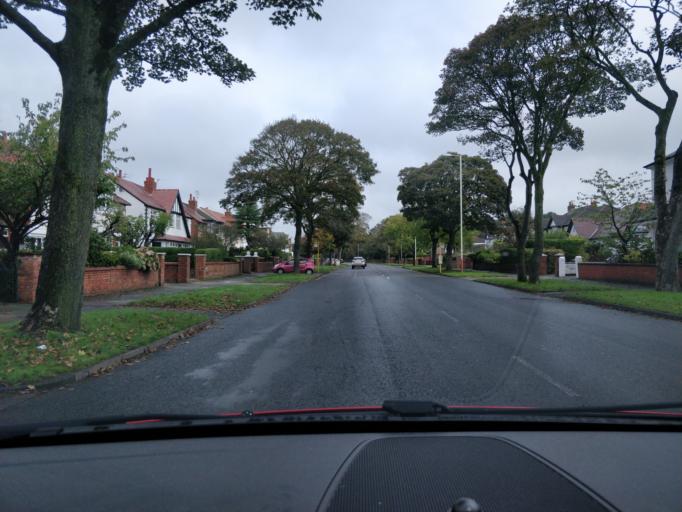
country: GB
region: England
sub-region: Sefton
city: Southport
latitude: 53.6046
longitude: -3.0312
